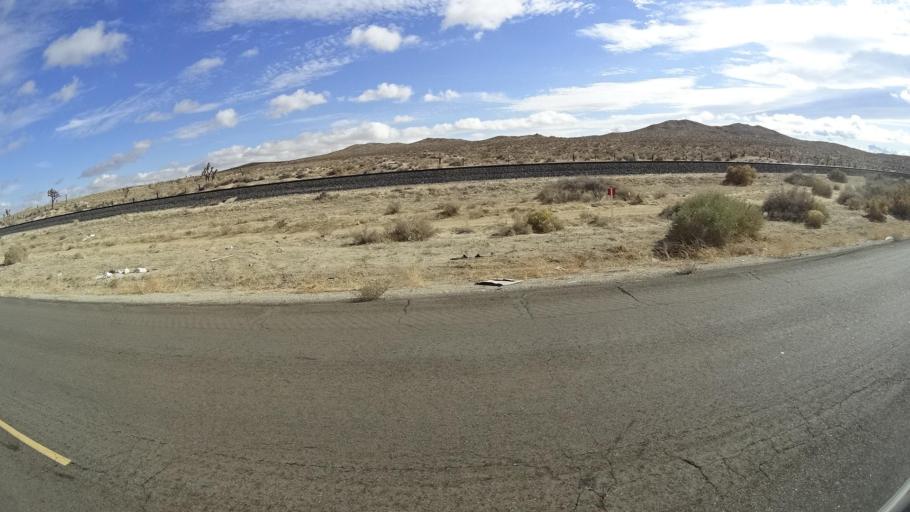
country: US
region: California
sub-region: Kern County
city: Rosamond
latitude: 34.8973
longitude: -118.1599
